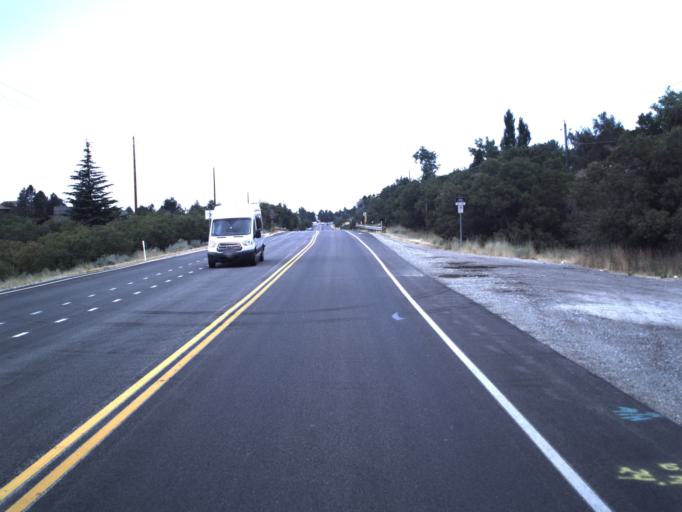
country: US
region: Utah
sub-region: Salt Lake County
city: Granite
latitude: 40.5899
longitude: -111.7938
